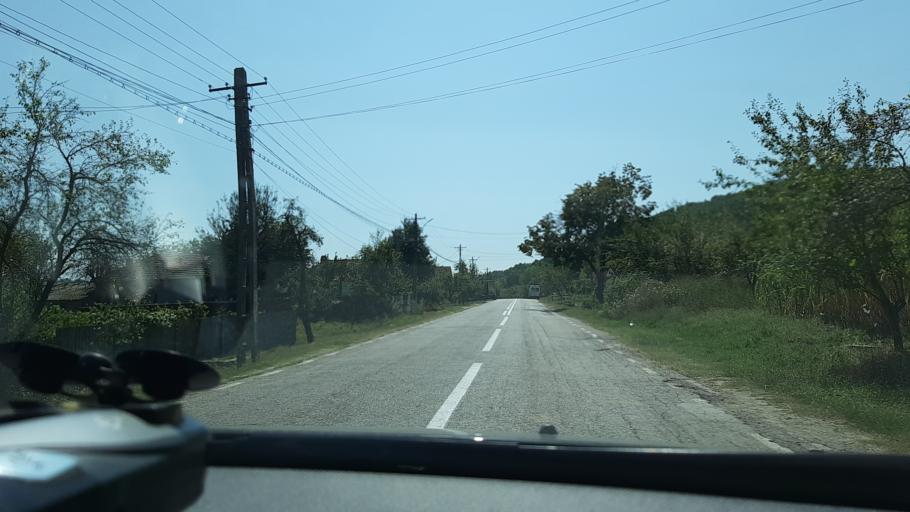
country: RO
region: Gorj
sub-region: Comuna Hurezani
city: Hurezani
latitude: 44.8288
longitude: 23.6432
